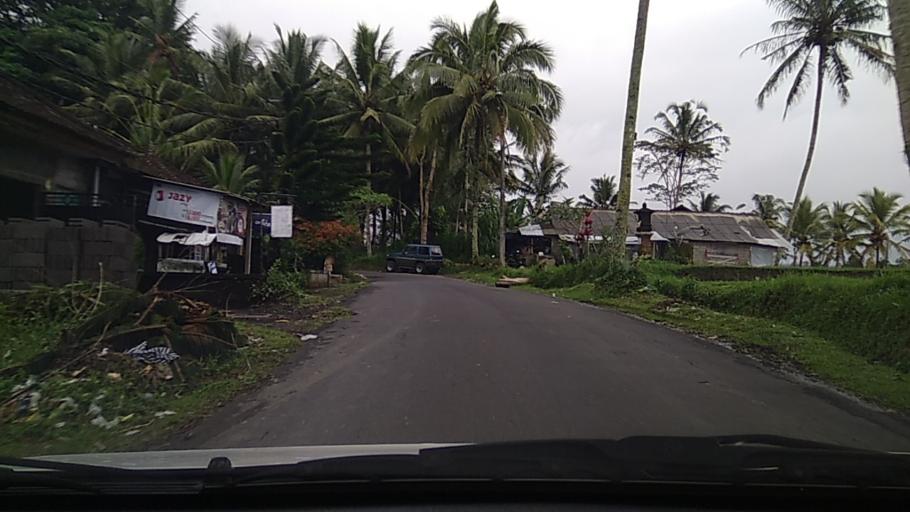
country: ID
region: Bali
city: Banjar Dujung Kaja
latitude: -8.4141
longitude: 115.2950
